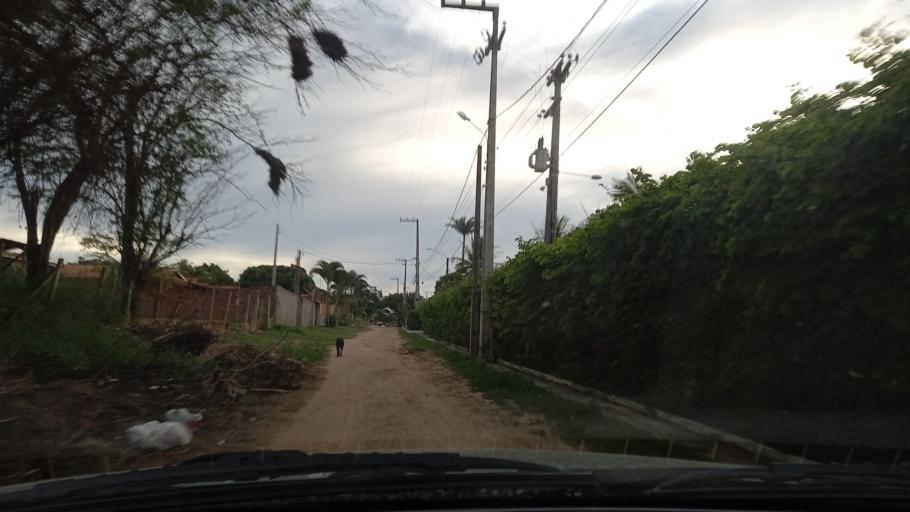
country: BR
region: Pernambuco
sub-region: Gravata
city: Gravata
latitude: -8.1954
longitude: -35.5826
